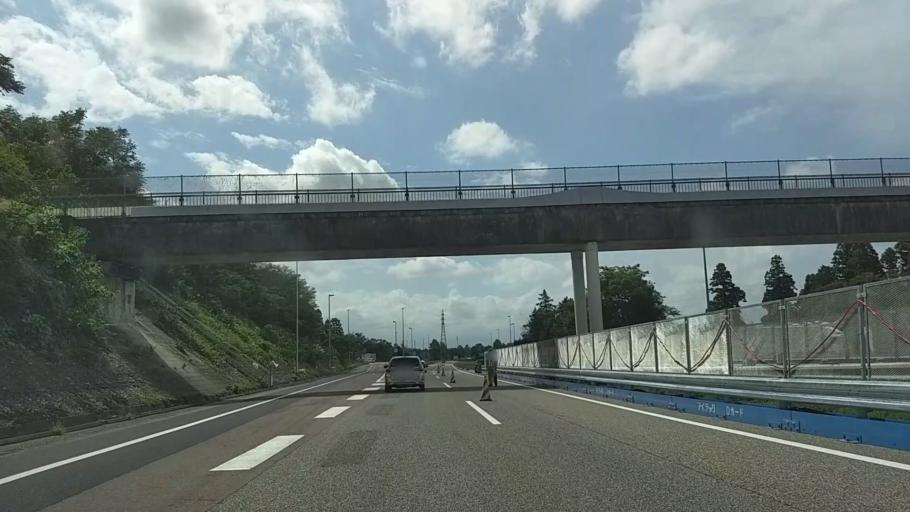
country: JP
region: Toyama
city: Takaoka
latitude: 36.6716
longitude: 137.0323
